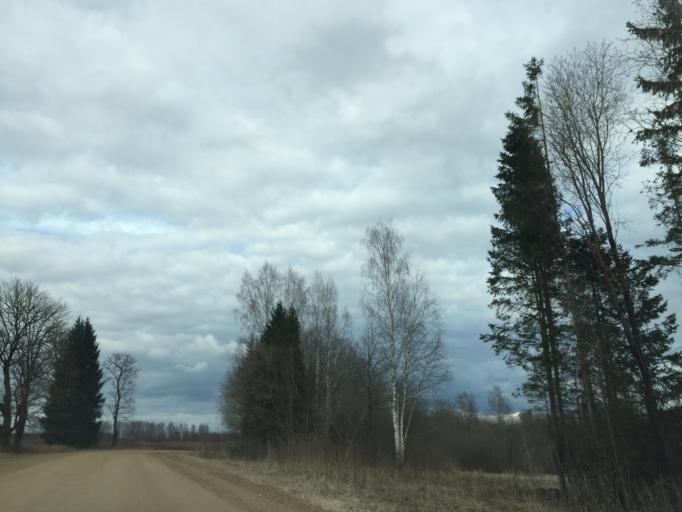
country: LV
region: Lielvarde
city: Lielvarde
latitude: 56.5199
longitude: 24.7552
